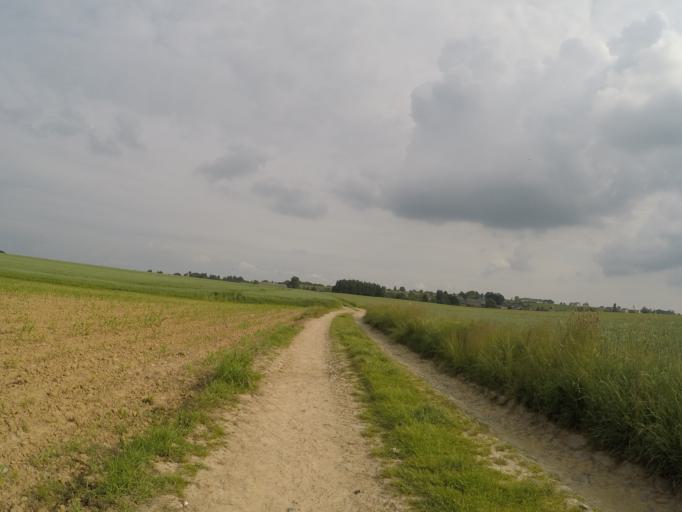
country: BE
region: Wallonia
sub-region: Province de Namur
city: Ciney
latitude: 50.3171
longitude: 5.0563
